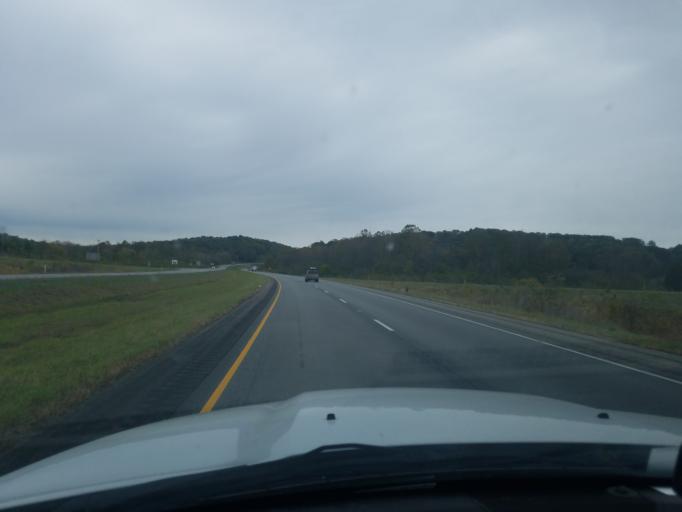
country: US
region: Indiana
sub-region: Dubois County
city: Ferdinand
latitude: 38.2253
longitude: -86.6992
